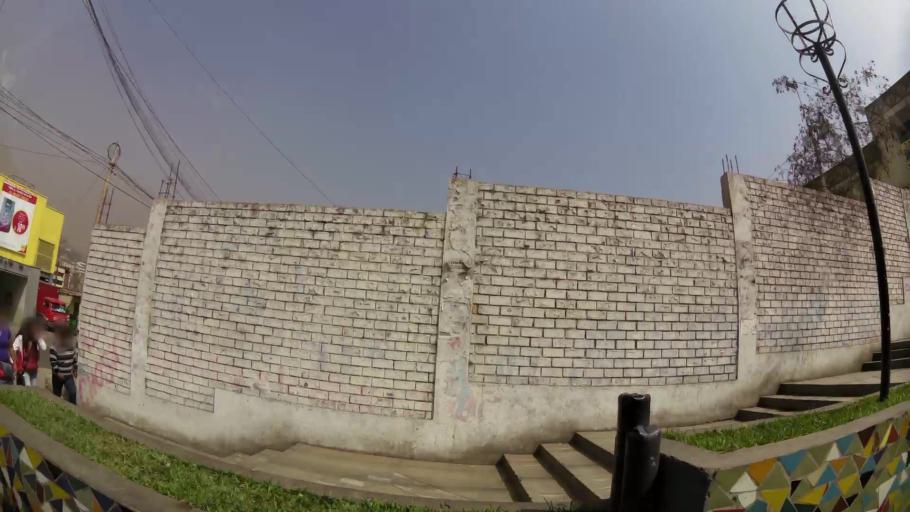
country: PE
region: Lima
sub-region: Lima
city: Asentamiento Humano Nicolas de Pierola
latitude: -11.9383
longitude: -76.6963
